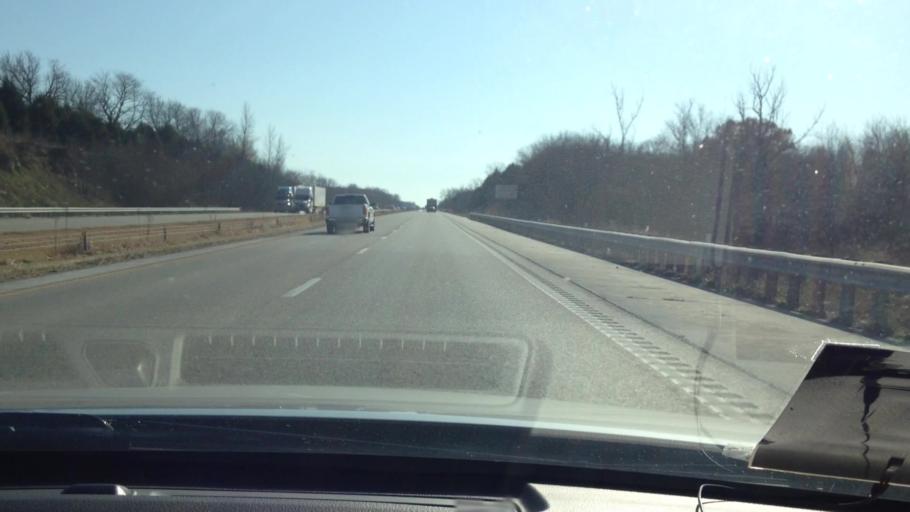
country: US
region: Missouri
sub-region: Platte County
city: Platte City
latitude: 39.4665
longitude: -94.7879
